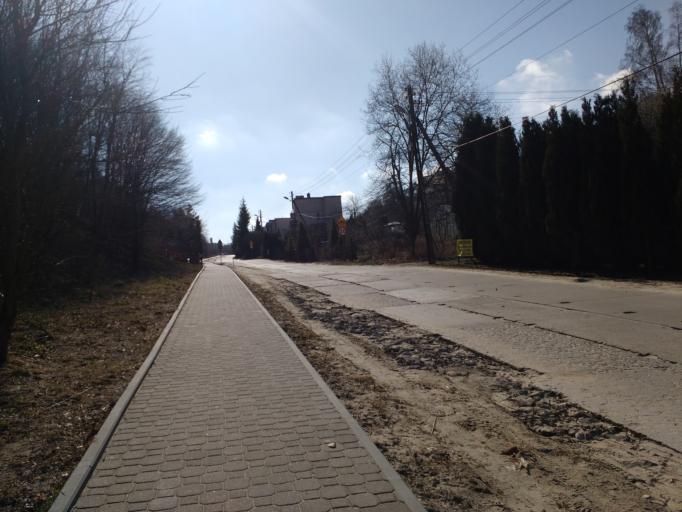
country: PL
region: Pomeranian Voivodeship
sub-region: Gdynia
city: Wielki Kack
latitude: 54.4763
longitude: 18.5116
